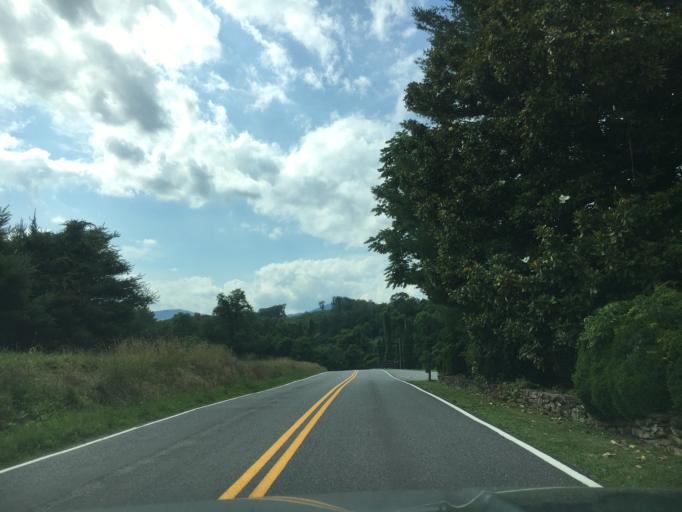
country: US
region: Virginia
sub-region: Roanoke County
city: Narrows
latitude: 37.1387
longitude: -79.9823
